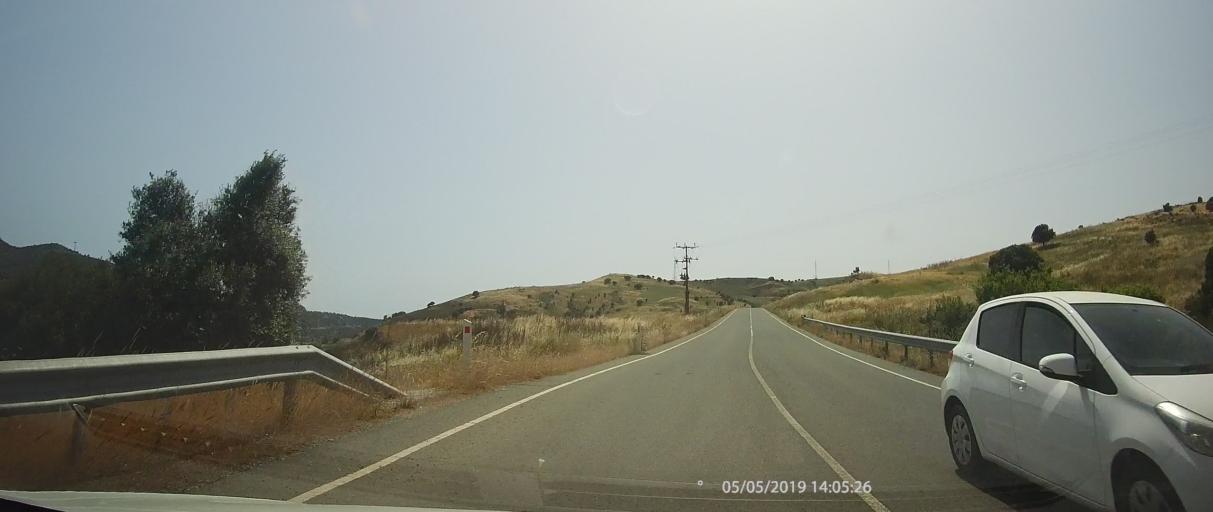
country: CY
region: Limassol
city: Pissouri
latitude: 34.7534
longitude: 32.6137
